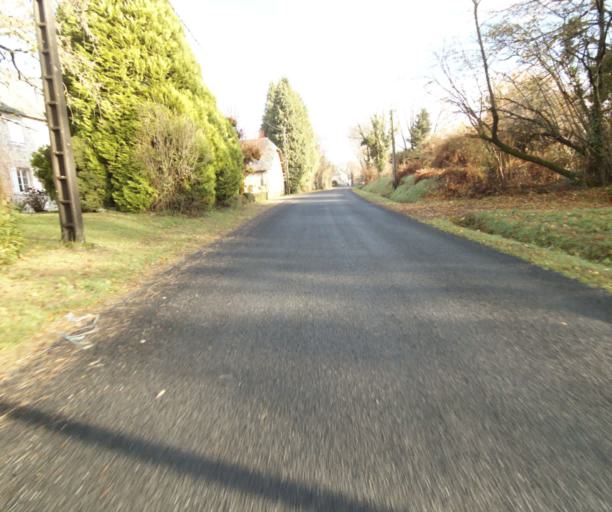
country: FR
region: Limousin
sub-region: Departement de la Correze
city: Saint-Mexant
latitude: 45.2502
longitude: 1.6238
